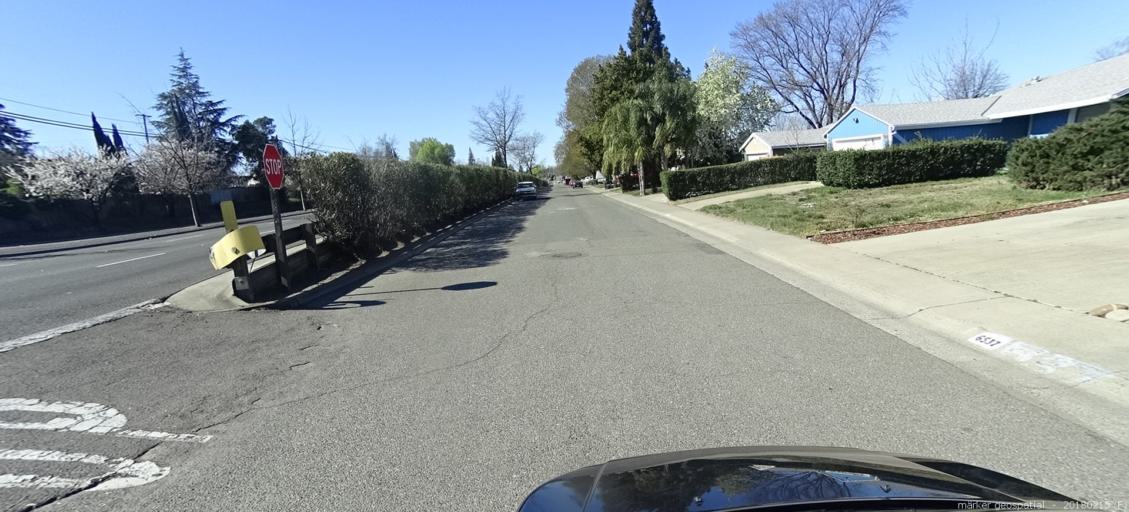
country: US
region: California
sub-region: Sacramento County
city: Foothill Farms
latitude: 38.6637
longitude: -121.3116
